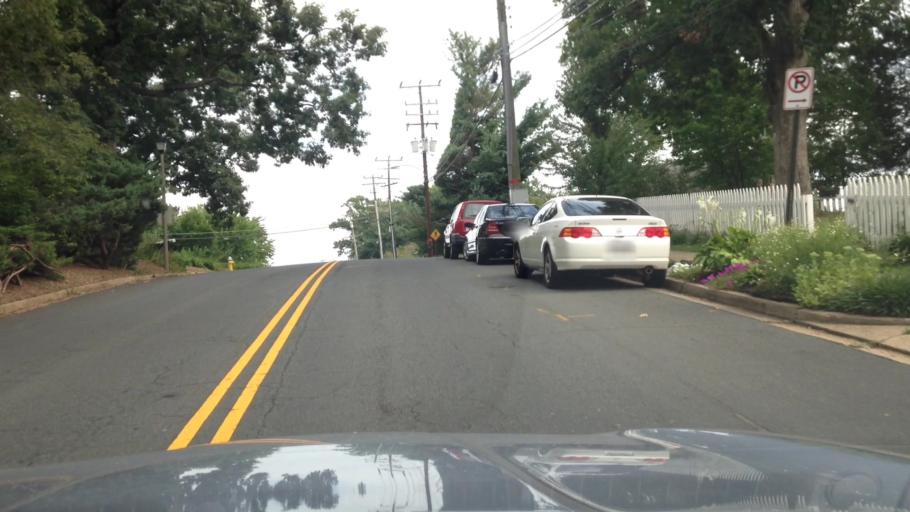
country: US
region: Virginia
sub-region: City of Falls Church
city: Falls Church
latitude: 38.9026
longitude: -77.1589
